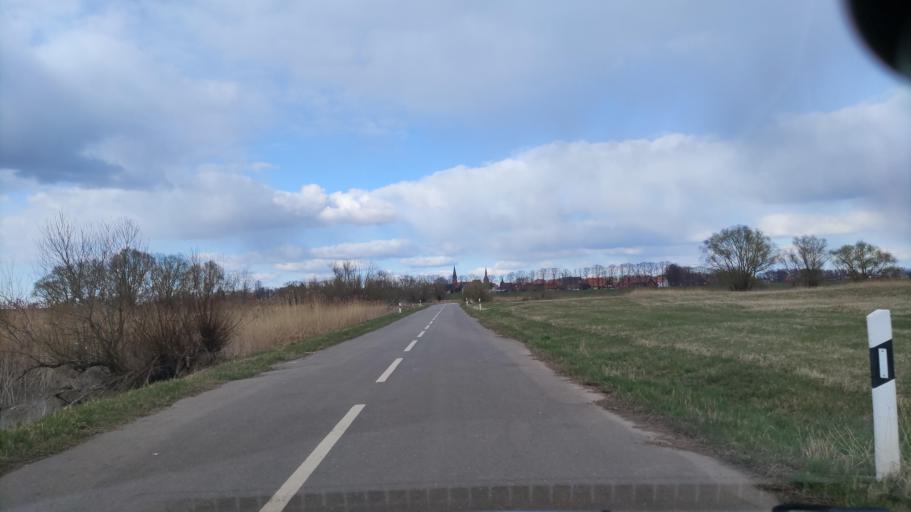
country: DE
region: Mecklenburg-Vorpommern
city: Domitz
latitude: 53.1357
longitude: 11.2403
